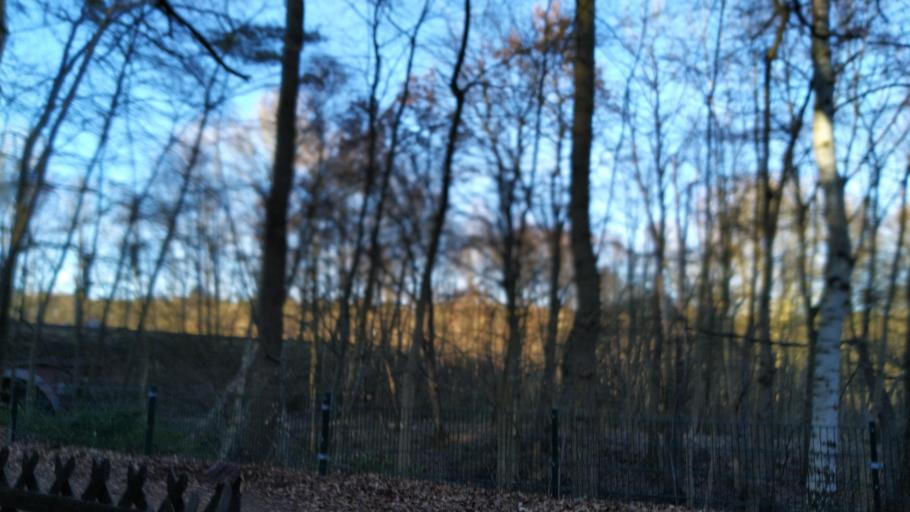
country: DE
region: Schleswig-Holstein
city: Bad Schwartau
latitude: 53.9239
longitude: 10.7123
